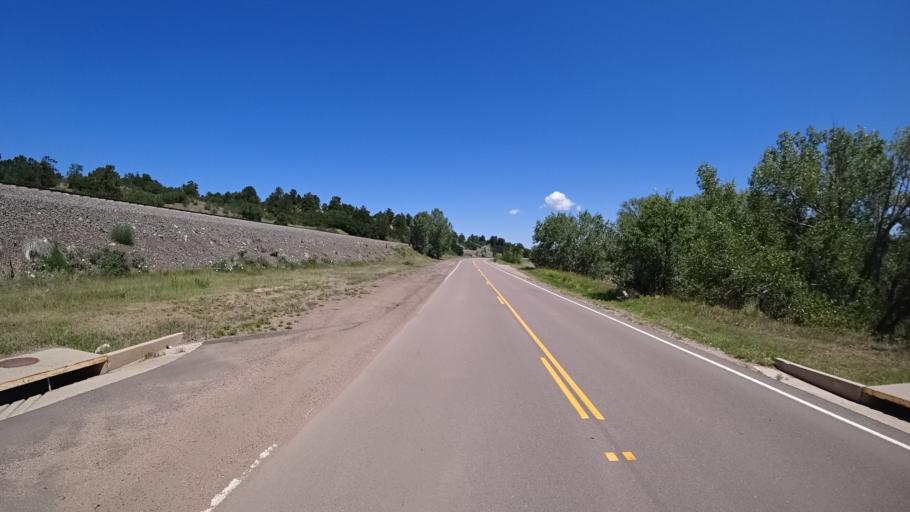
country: US
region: Colorado
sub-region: El Paso County
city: Air Force Academy
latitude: 38.9223
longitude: -104.8197
